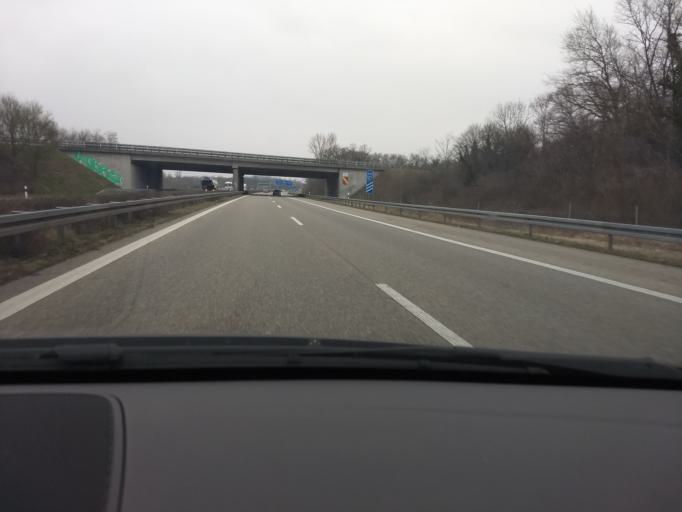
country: FR
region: Alsace
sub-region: Departement du Haut-Rhin
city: Ottmarsheim
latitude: 47.7757
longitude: 7.5360
